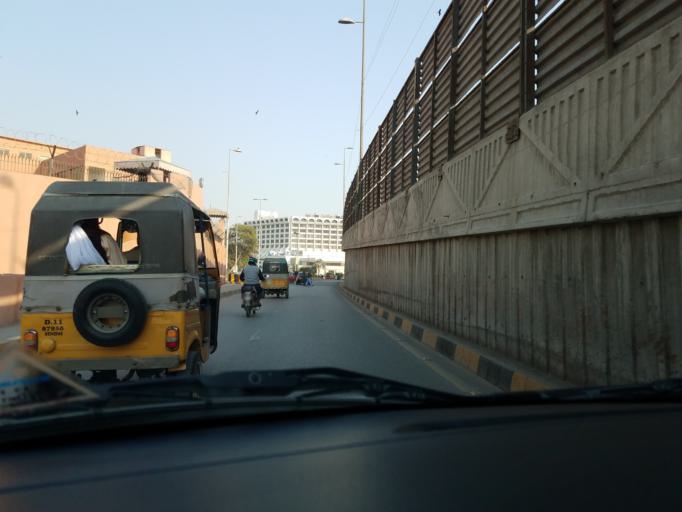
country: PK
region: Sindh
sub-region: Karachi District
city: Karachi
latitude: 24.8560
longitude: 67.0370
